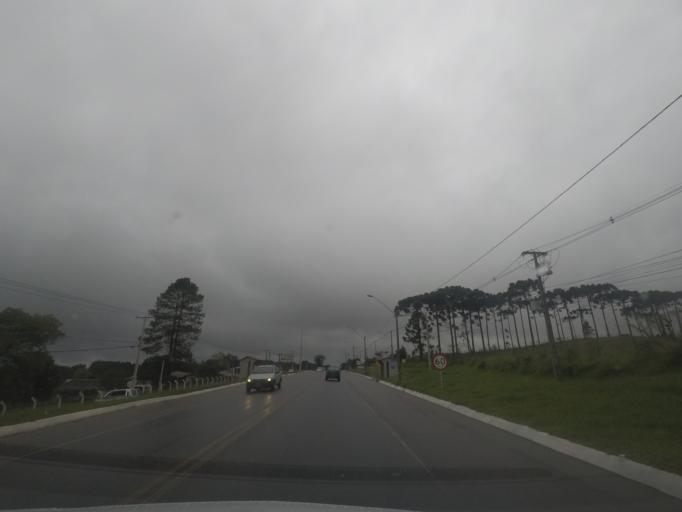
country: BR
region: Parana
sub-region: Colombo
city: Colombo
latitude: -25.3453
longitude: -49.1604
